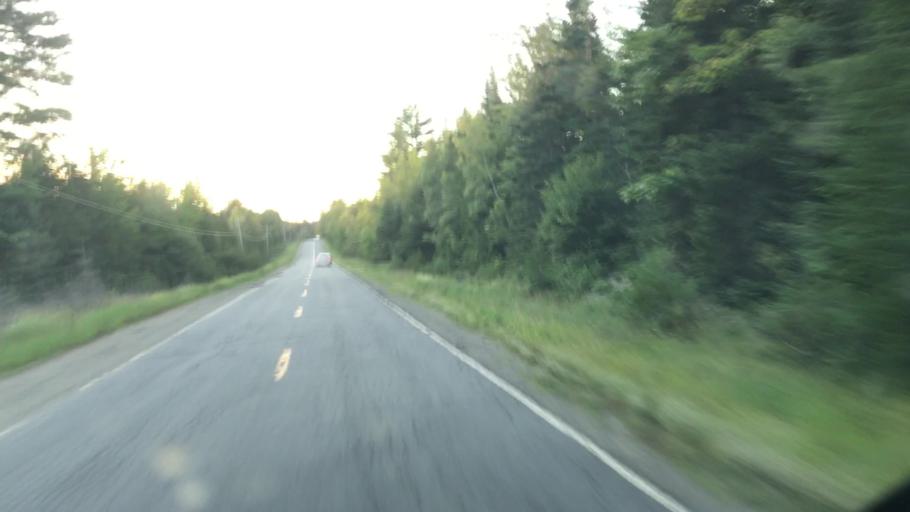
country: US
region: Maine
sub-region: Penobscot County
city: Medway
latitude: 45.6018
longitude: -68.2501
